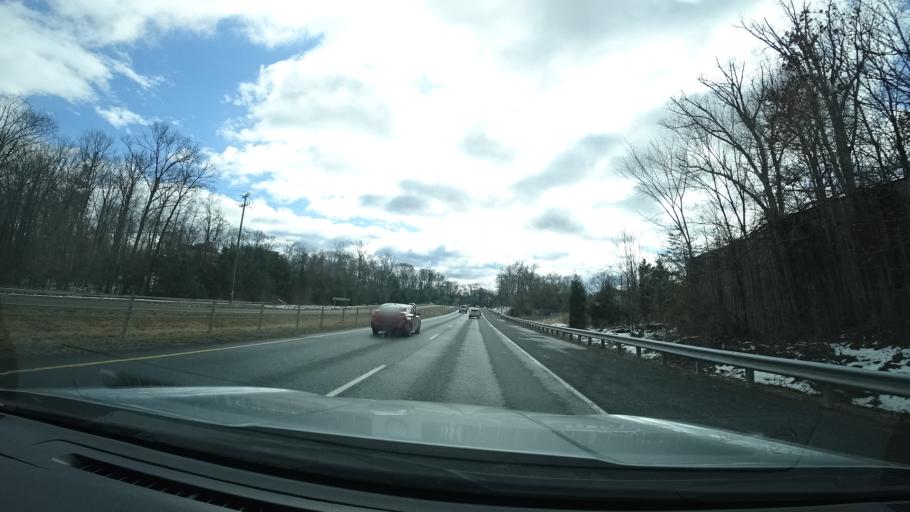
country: US
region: Virginia
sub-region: Fairfax County
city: Dranesville
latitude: 38.9873
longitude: -77.3600
